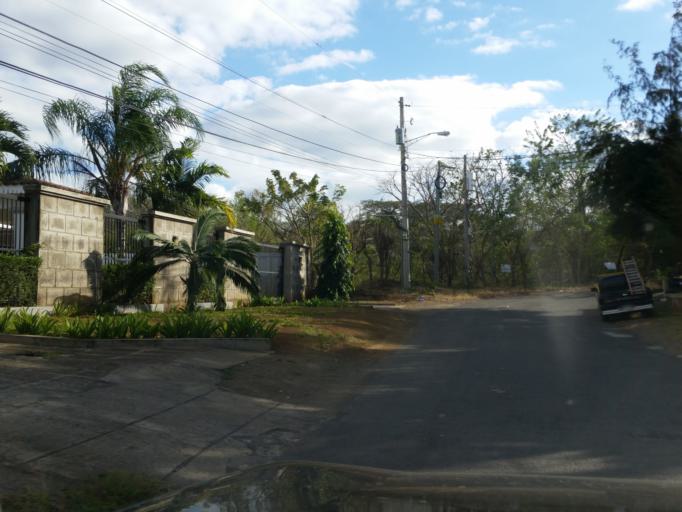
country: NI
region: Managua
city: Managua
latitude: 12.0783
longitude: -86.2481
